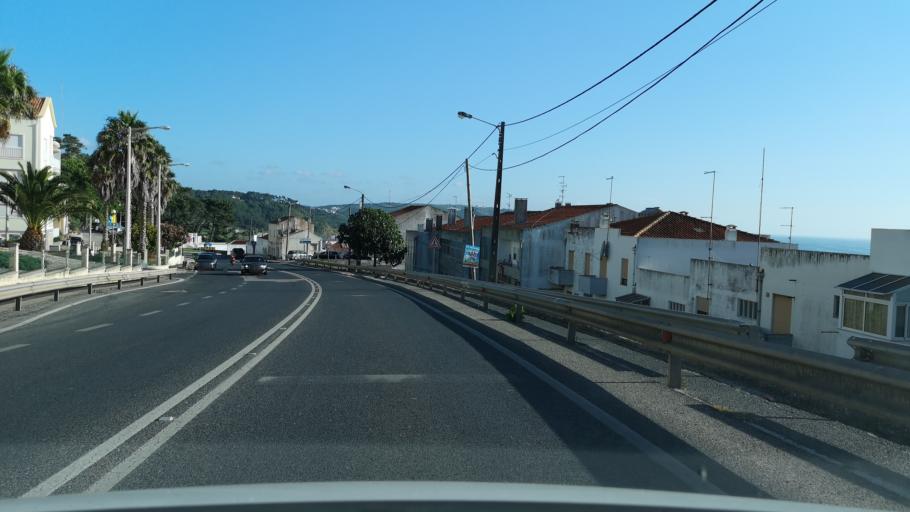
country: PT
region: Leiria
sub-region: Nazare
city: Nazare
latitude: 39.6029
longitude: -9.0677
